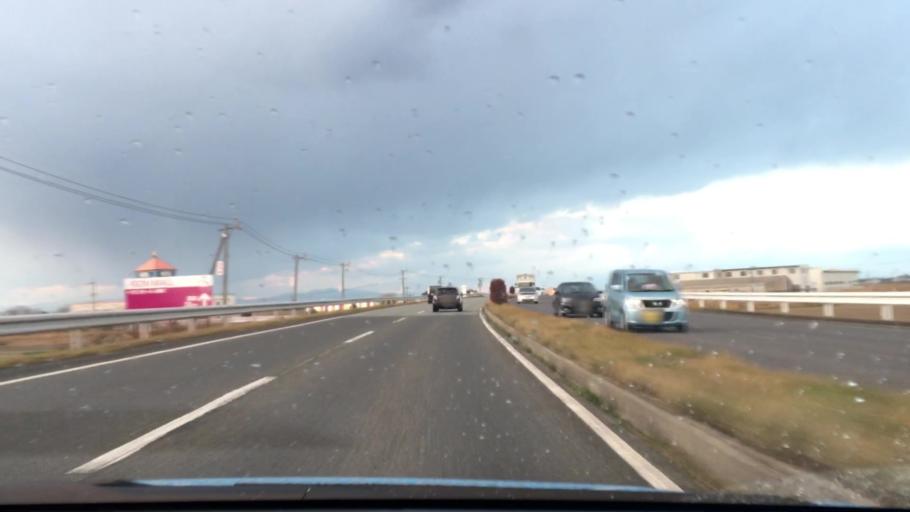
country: JP
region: Mie
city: Ise
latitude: 34.5438
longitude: 136.6615
